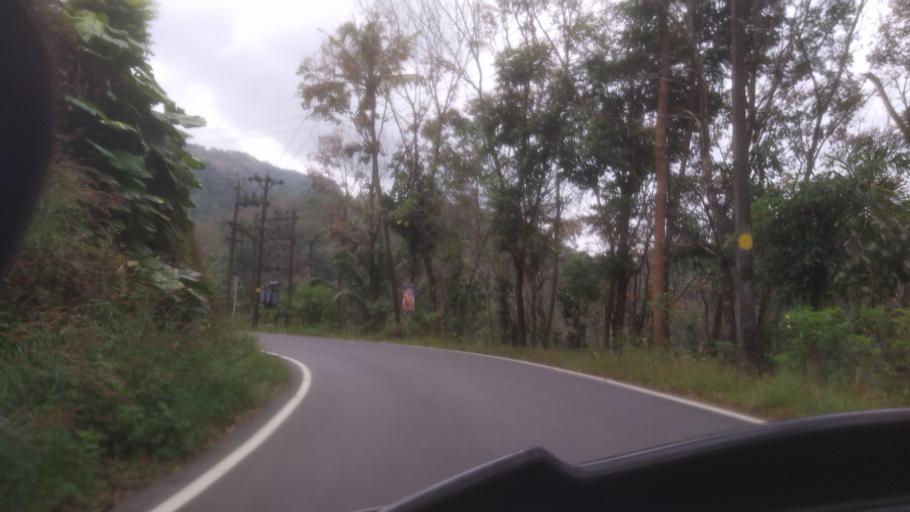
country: IN
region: Kerala
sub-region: Idukki
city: Idukki
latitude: 9.9724
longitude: 76.9992
